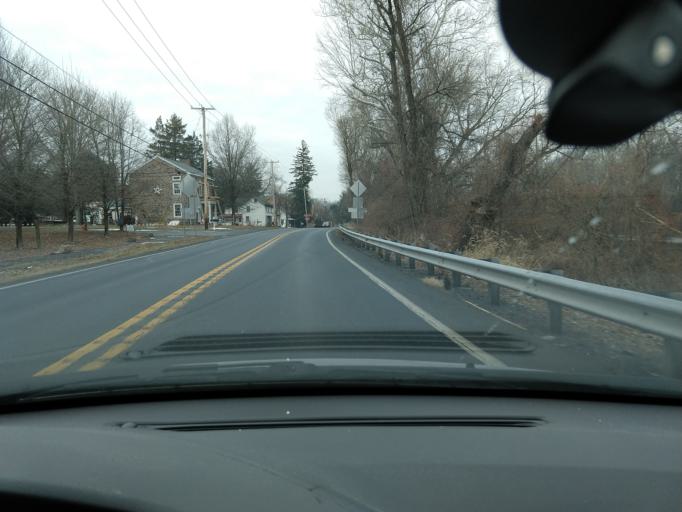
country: US
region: Pennsylvania
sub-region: Berks County
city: Amity Gardens
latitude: 40.2501
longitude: -75.7268
